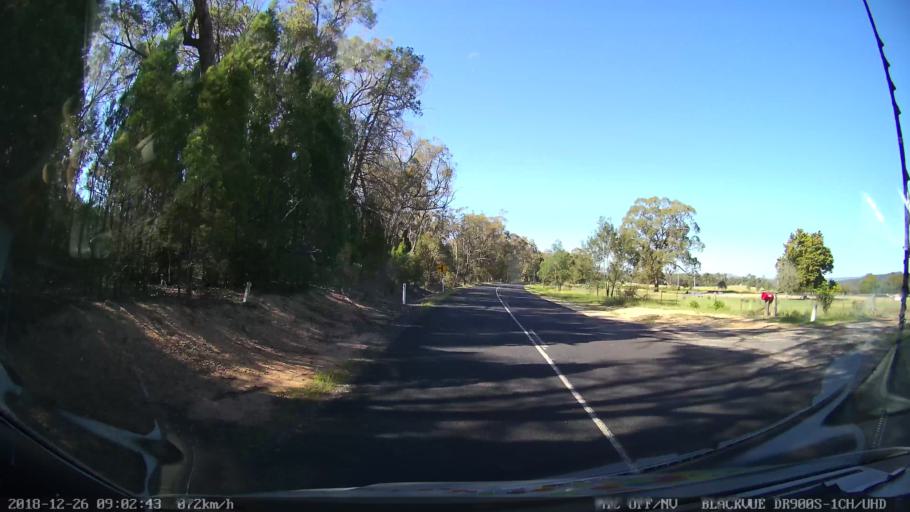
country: AU
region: New South Wales
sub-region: Mid-Western Regional
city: Kandos
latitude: -32.6558
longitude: 150.0177
